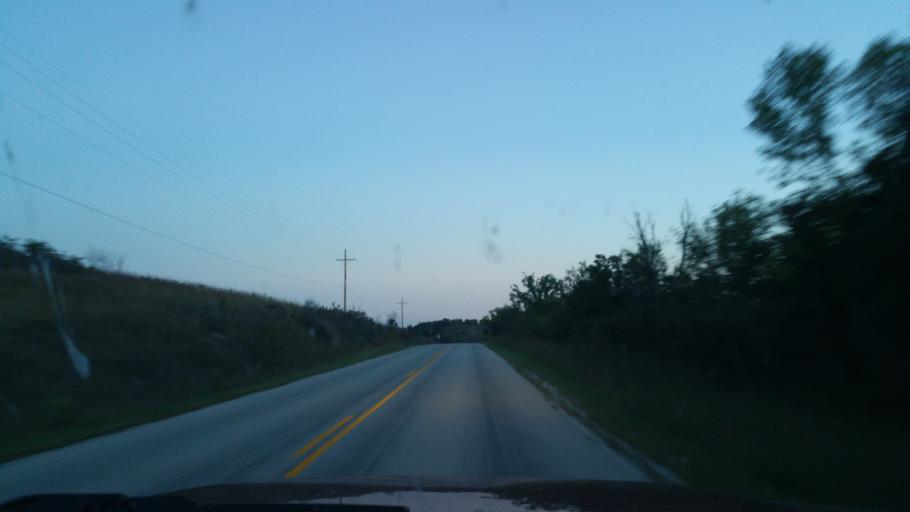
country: US
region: Kansas
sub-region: Riley County
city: Manhattan
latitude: 39.2602
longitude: -96.5698
